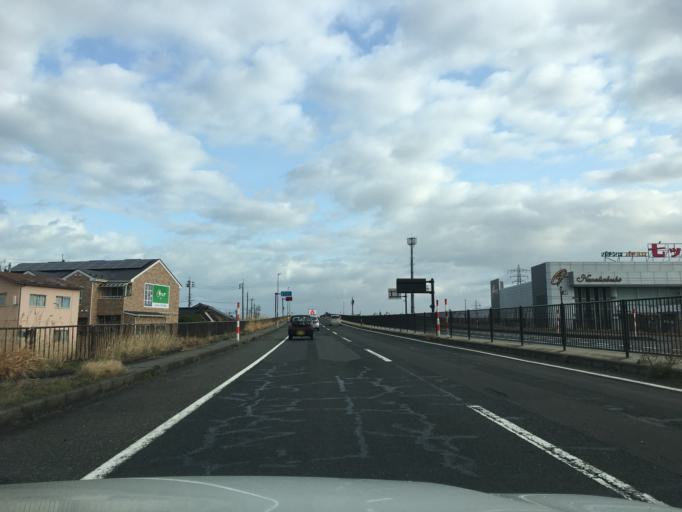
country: JP
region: Yamagata
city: Sakata
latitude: 38.9097
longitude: 139.8575
